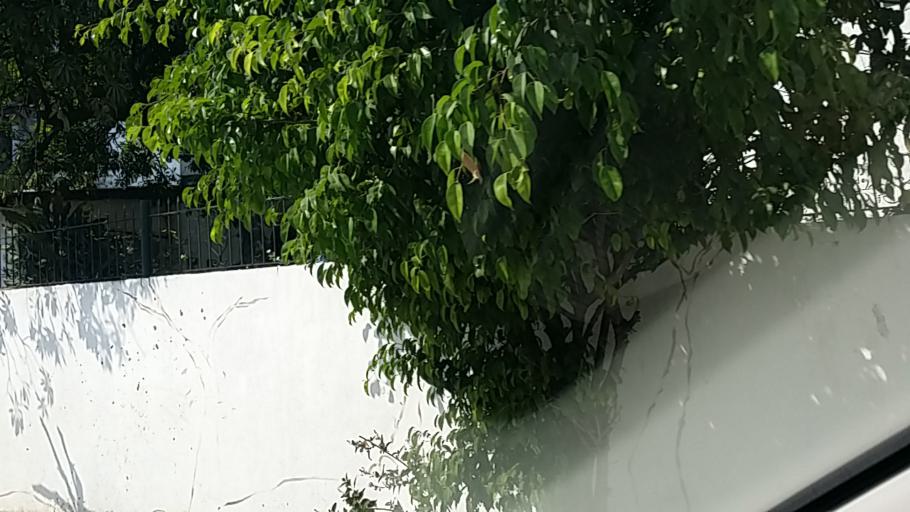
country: PH
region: Metro Manila
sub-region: Mandaluyong
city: Mandaluyong City
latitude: 14.5735
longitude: 121.0411
